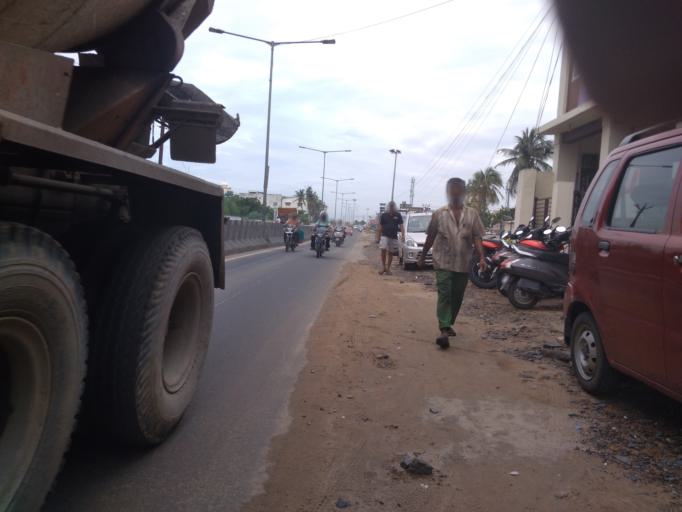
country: IN
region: Tamil Nadu
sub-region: Kancheepuram
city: Injambakkam
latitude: 12.9009
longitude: 80.2266
